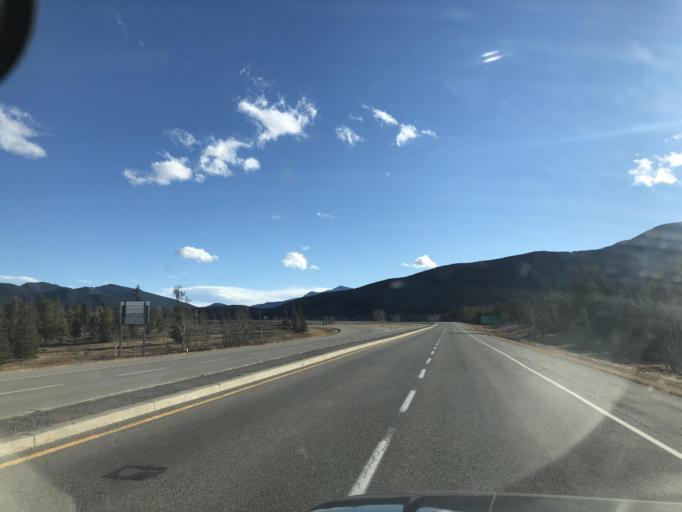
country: CA
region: Alberta
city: Canmore
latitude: 51.0830
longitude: -115.0621
